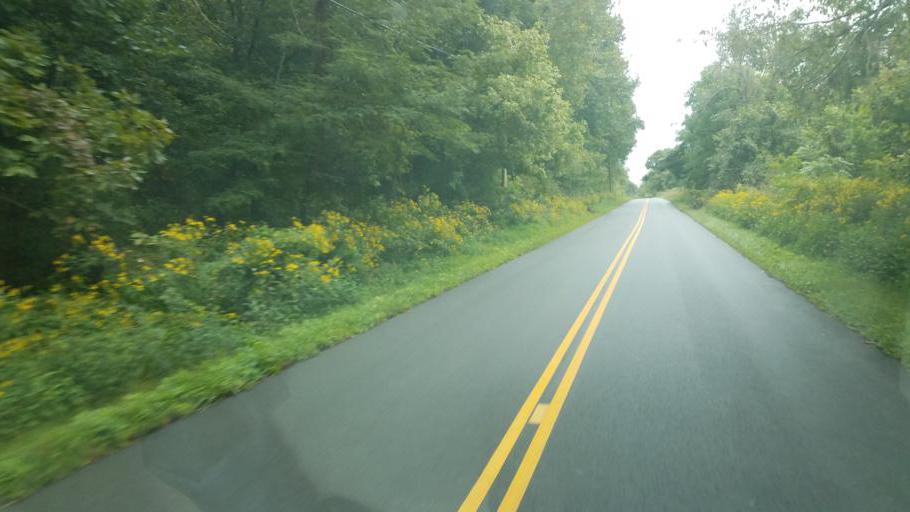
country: US
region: Ohio
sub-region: Scioto County
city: Franklin Furnace
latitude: 38.6515
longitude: -82.8503
